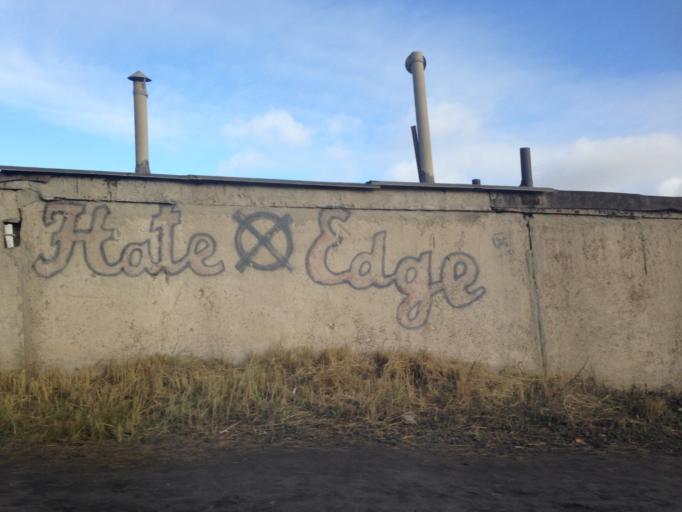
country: RU
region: Ulyanovsk
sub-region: Ulyanovskiy Rayon
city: Ulyanovsk
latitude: 54.2801
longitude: 48.2749
